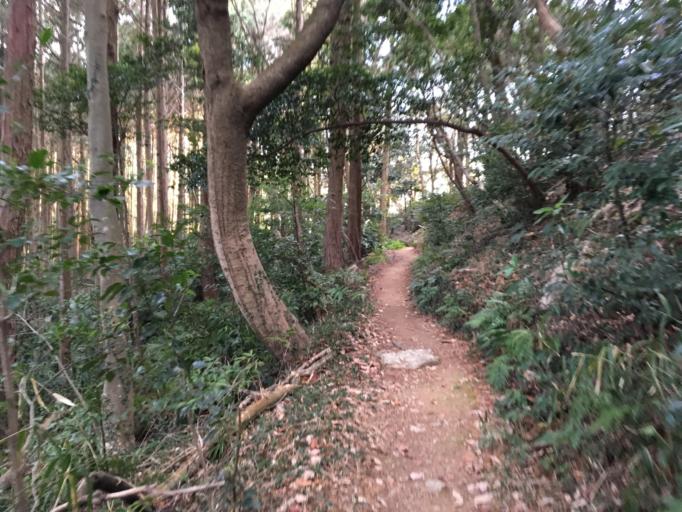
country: JP
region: Aichi
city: Toyohashi
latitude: 34.7359
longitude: 137.4493
